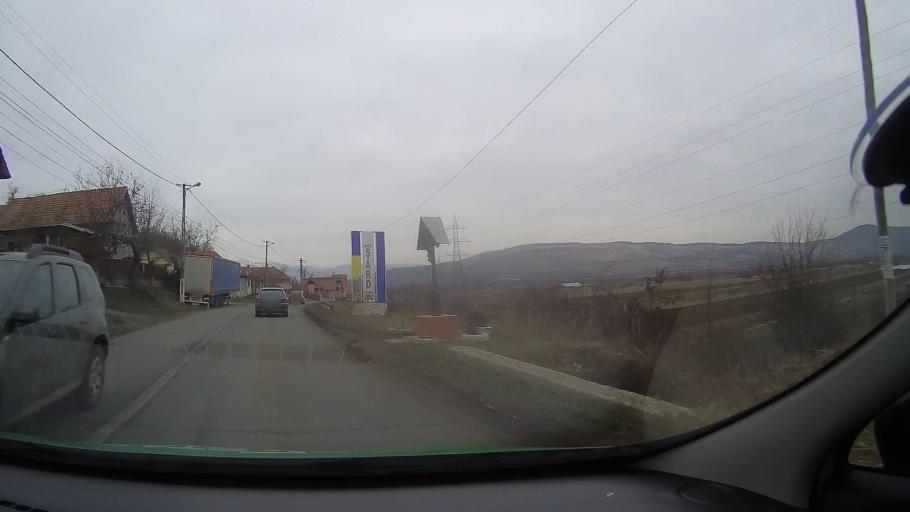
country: RO
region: Alba
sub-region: Comuna Ighiu
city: Sard
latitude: 46.1158
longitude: 23.5384
